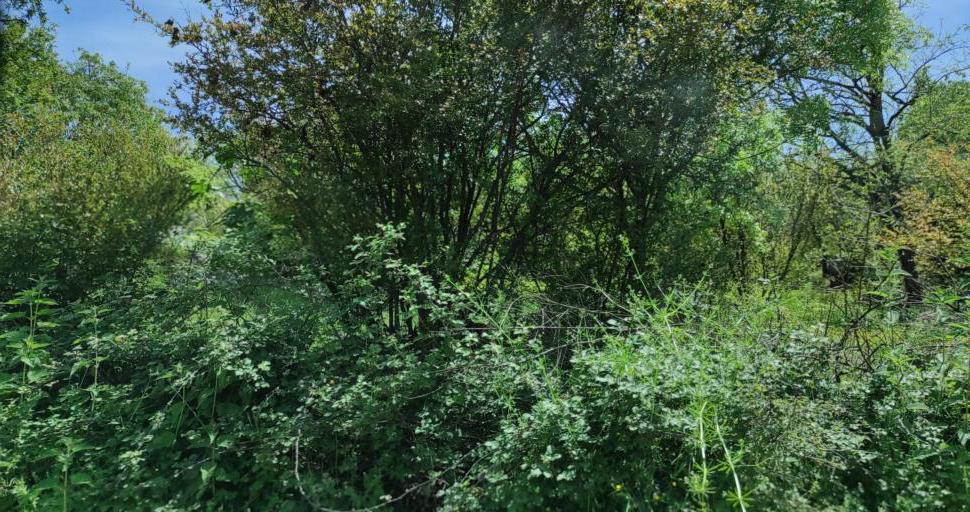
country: AL
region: Shkoder
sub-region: Rrethi i Malesia e Madhe
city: Gruemire
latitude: 42.1398
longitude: 19.5468
